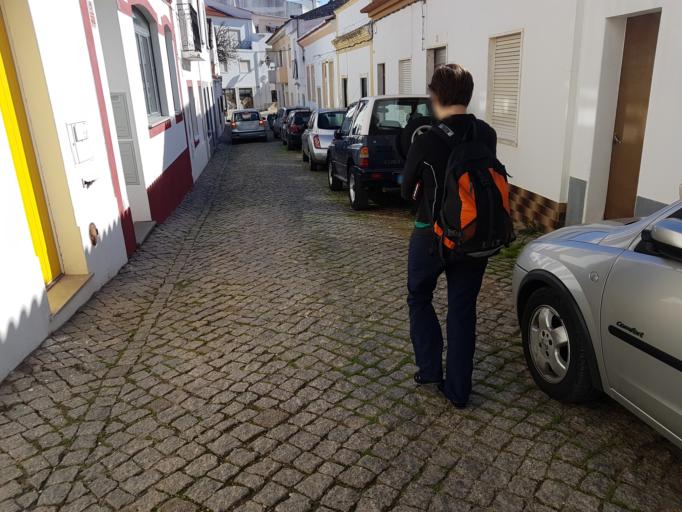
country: PT
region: Faro
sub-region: Lagos
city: Lagos
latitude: 37.1013
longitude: -8.6748
